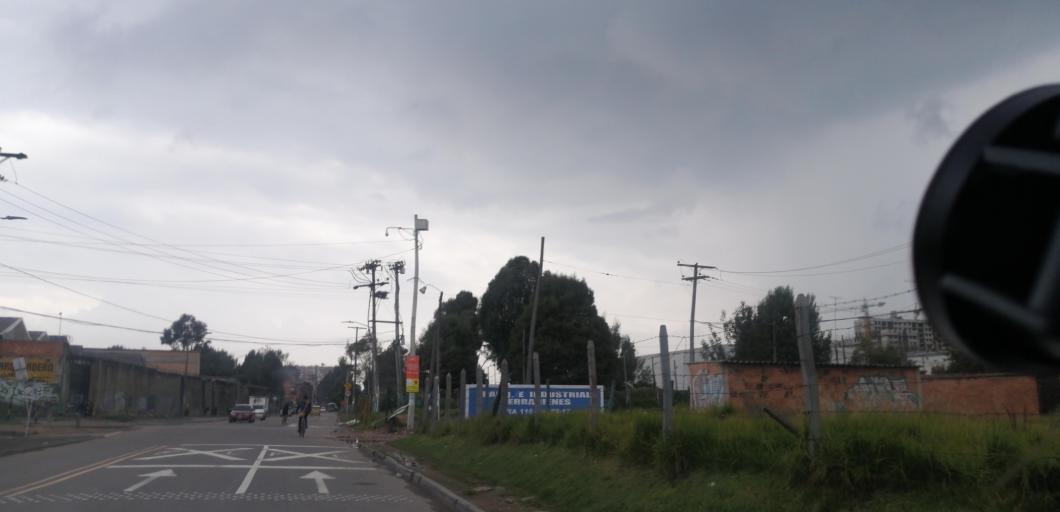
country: CO
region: Cundinamarca
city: Funza
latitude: 4.6870
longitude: -74.1503
